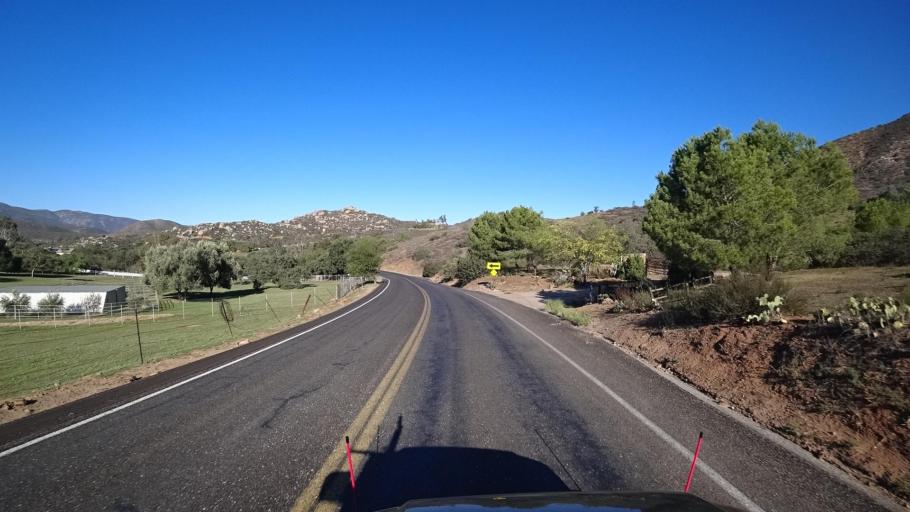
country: MX
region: Baja California
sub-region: Tijuana
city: Villa del Campo
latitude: 32.6229
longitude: -116.7484
